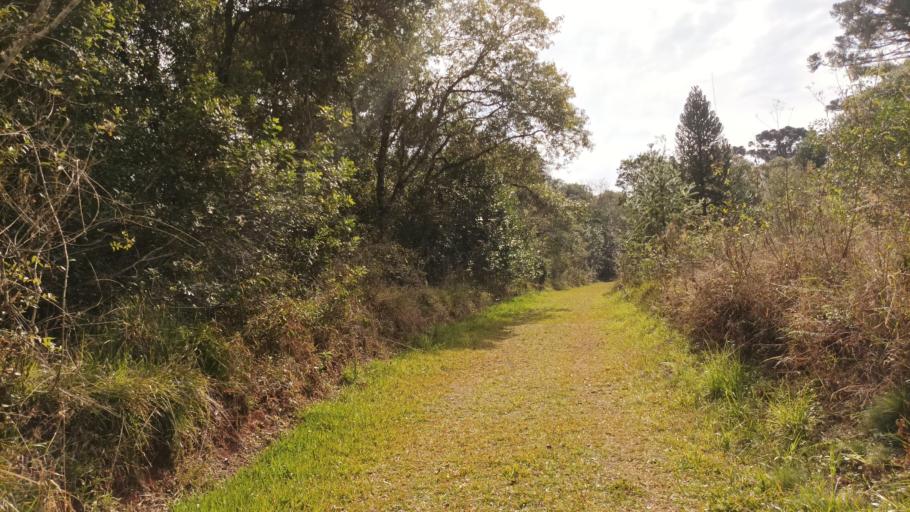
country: AR
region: Misiones
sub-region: Departamento de San Pedro
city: San Pedro
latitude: -26.6301
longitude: -54.1046
